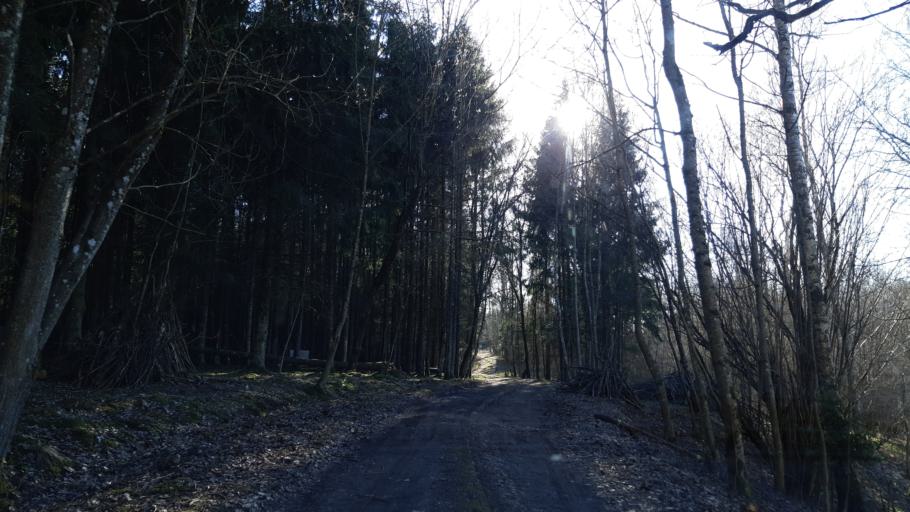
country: LT
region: Kauno apskritis
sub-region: Kaunas
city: Sargenai
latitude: 55.0305
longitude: 23.7748
